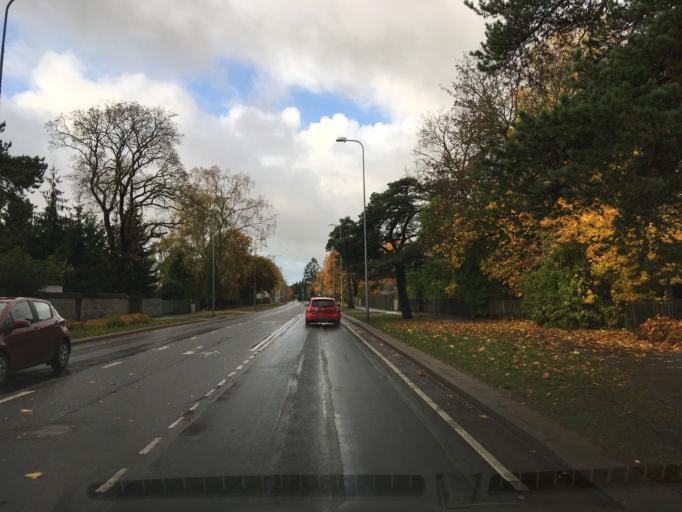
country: EE
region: Harju
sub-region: Saue vald
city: Laagri
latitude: 59.3796
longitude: 24.6577
